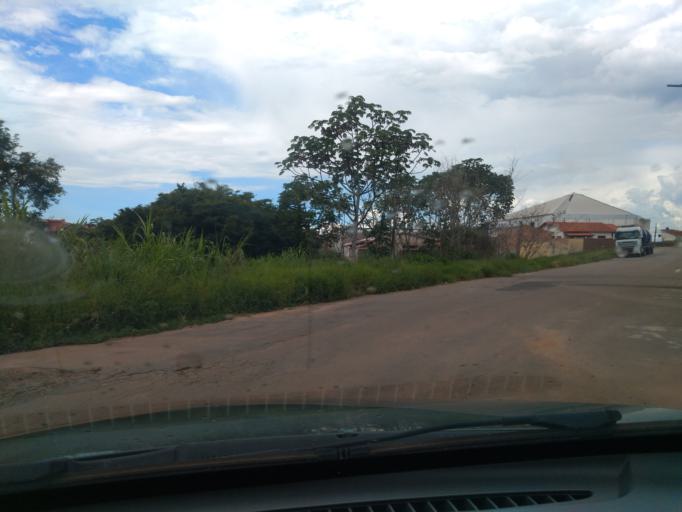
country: BR
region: Minas Gerais
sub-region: Tres Coracoes
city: Tres Coracoes
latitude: -21.6869
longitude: -45.2660
